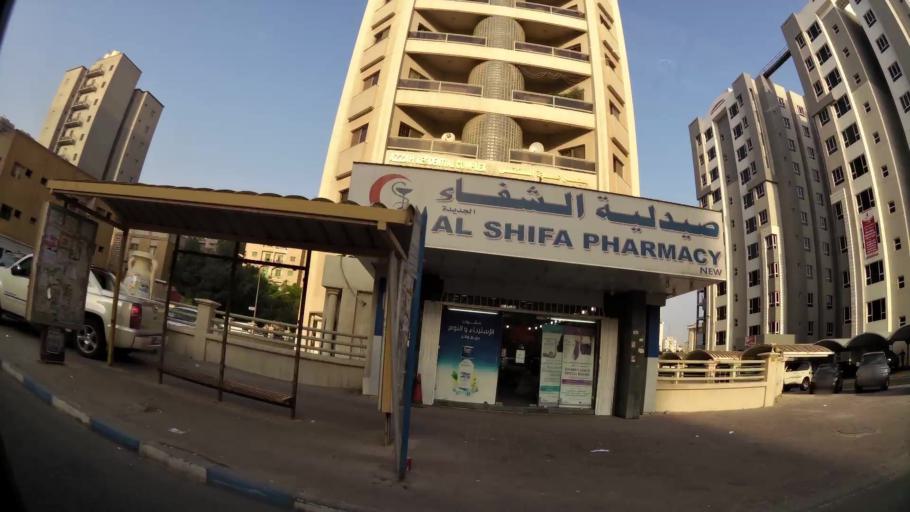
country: KW
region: Muhafazat Hawalli
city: As Salimiyah
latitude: 29.3291
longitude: 48.0554
